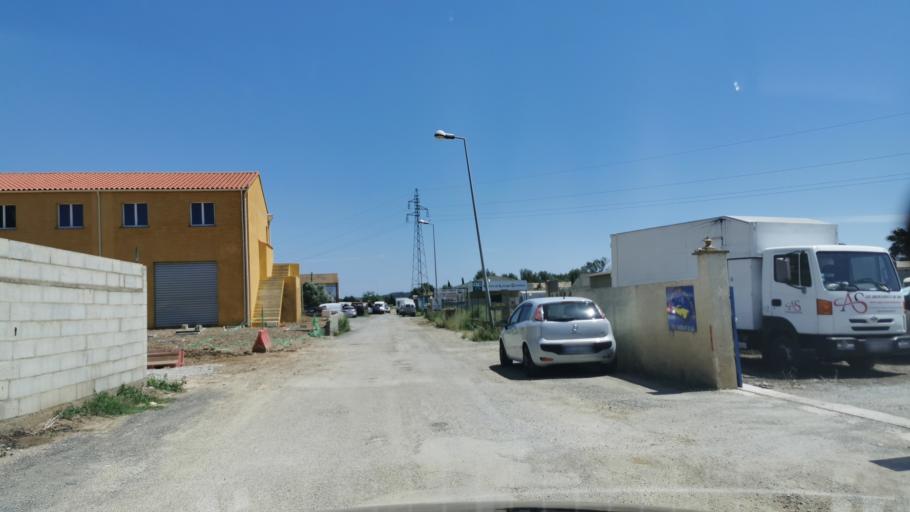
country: FR
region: Languedoc-Roussillon
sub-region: Departement de l'Aude
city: Canet
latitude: 43.2183
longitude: 2.8467
